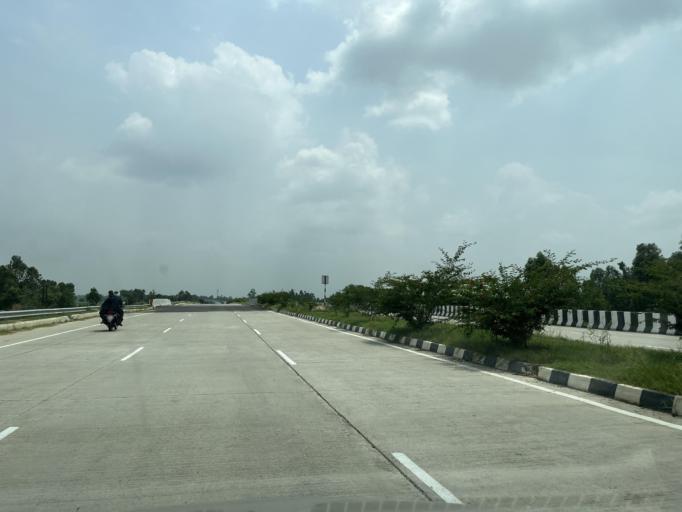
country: IN
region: Uttar Pradesh
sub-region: Bijnor
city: Nagina
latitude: 29.4297
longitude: 78.4161
